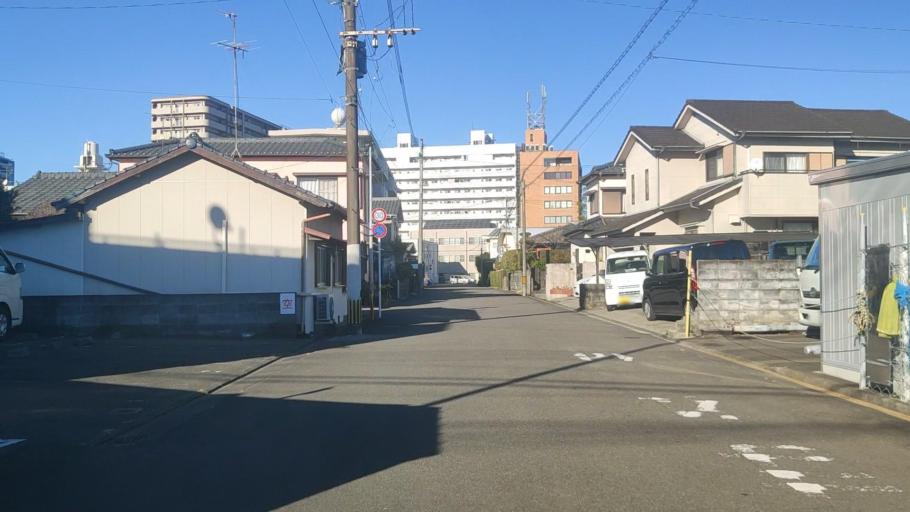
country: JP
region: Miyazaki
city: Miyazaki-shi
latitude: 31.9006
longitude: 131.4220
